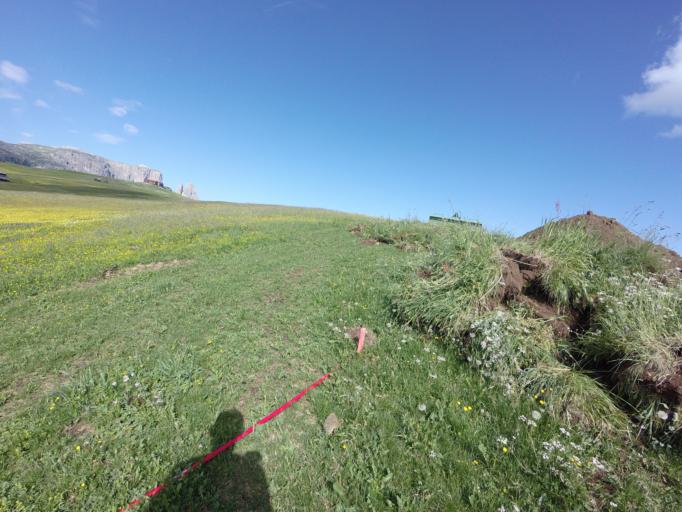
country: IT
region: Trentino-Alto Adige
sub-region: Bolzano
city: Ortisei
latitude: 46.5332
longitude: 11.6353
